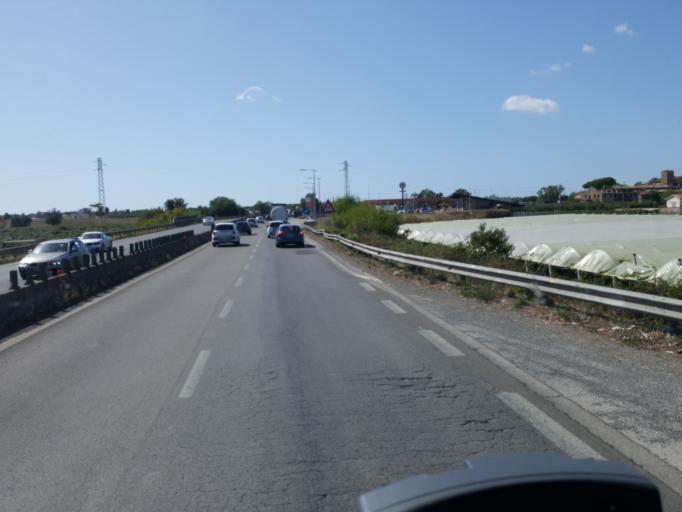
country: IT
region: Latium
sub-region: Provincia di Latina
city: Genio Civile
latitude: 41.5369
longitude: 12.7350
